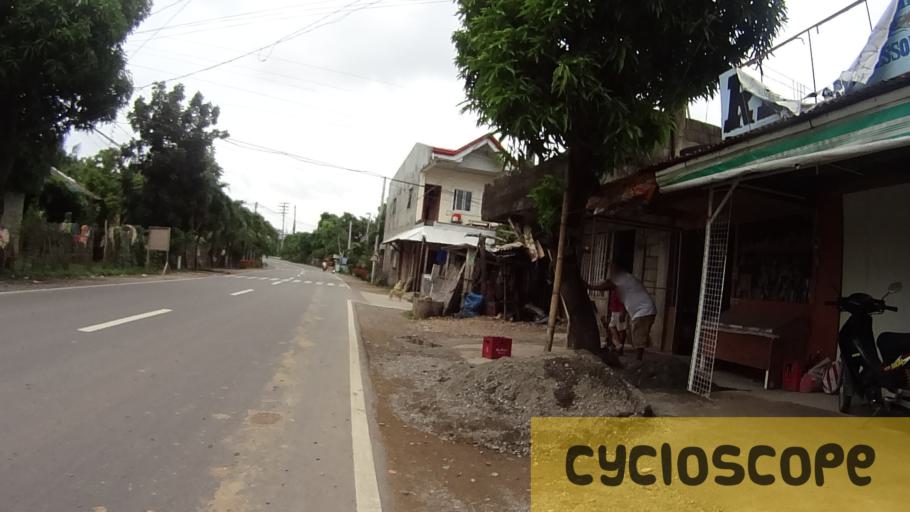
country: PH
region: Western Visayas
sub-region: Province of Aklan
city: Caticlan
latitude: 11.9320
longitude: 121.9606
